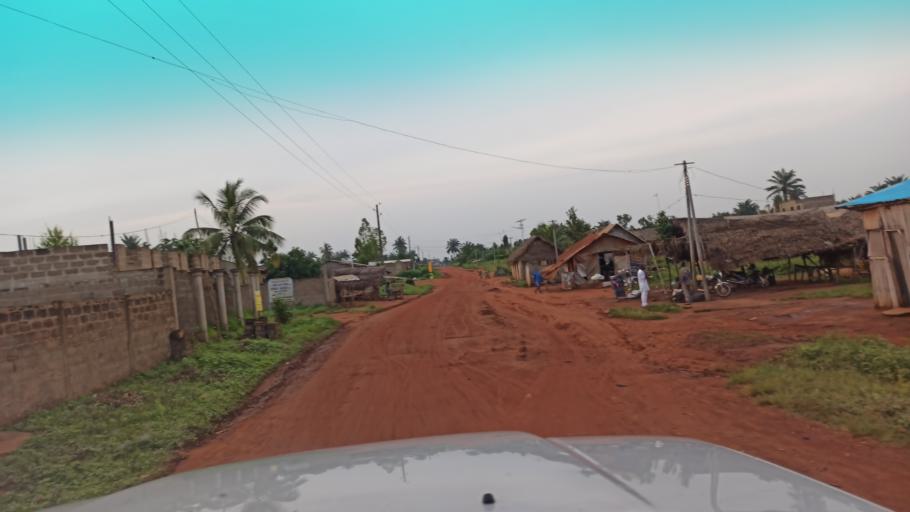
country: BJ
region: Queme
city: Porto-Novo
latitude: 6.5176
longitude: 2.6776
